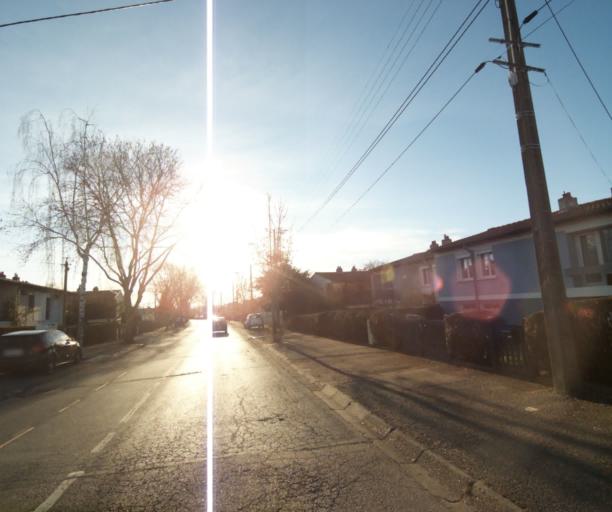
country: FR
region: Lorraine
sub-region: Departement de Meurthe-et-Moselle
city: Seichamps
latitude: 48.7148
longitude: 6.2585
